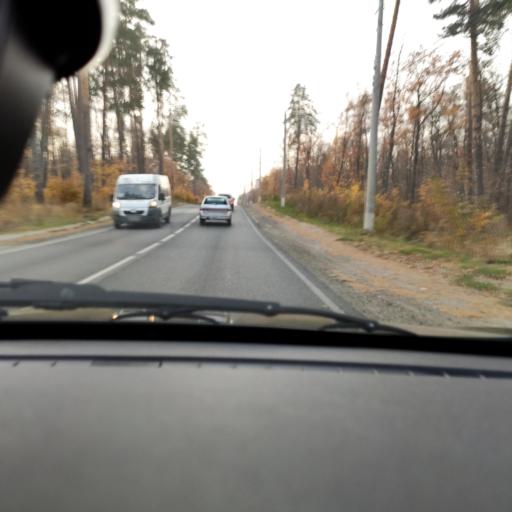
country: RU
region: Samara
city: Tol'yatti
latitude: 53.4918
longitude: 49.3040
